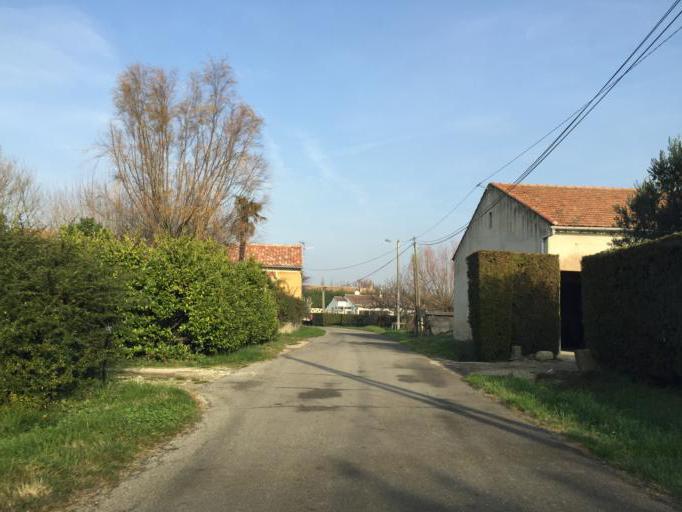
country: FR
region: Provence-Alpes-Cote d'Azur
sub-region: Departement du Vaucluse
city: Jonquieres
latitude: 44.1226
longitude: 4.8957
